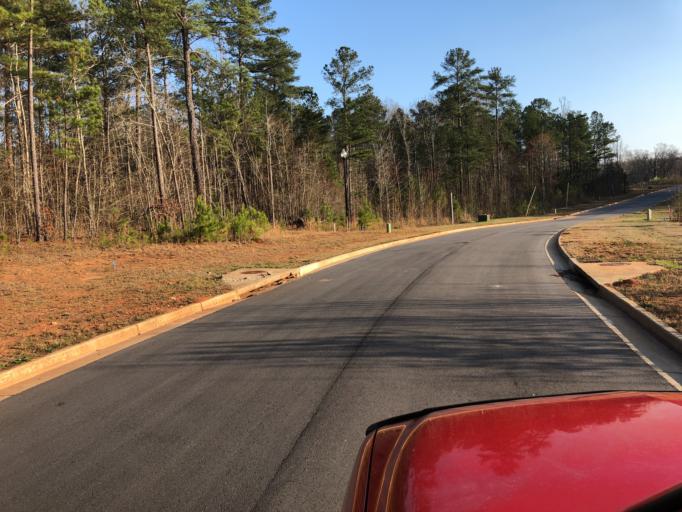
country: US
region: Georgia
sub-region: Henry County
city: McDonough
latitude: 33.4571
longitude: -84.1093
